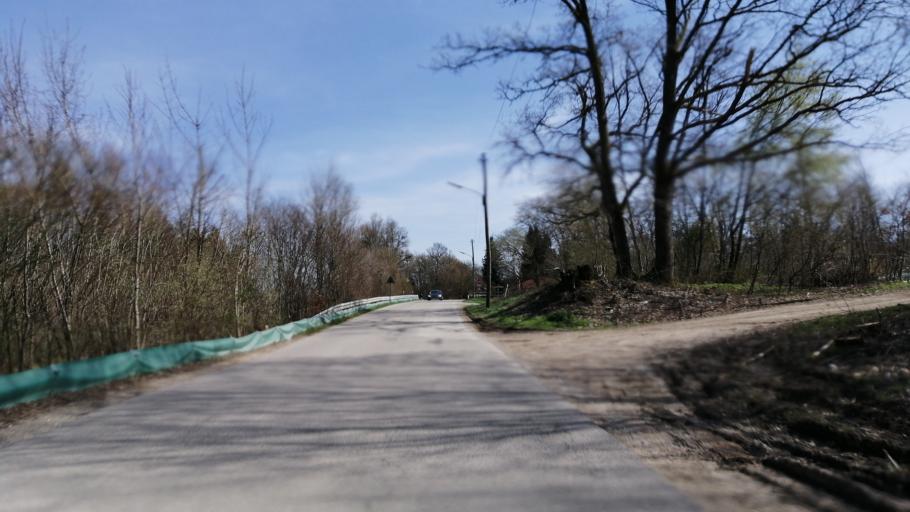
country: DE
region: Bavaria
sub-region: Upper Bavaria
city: Oberhaching
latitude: 48.0105
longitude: 11.5890
